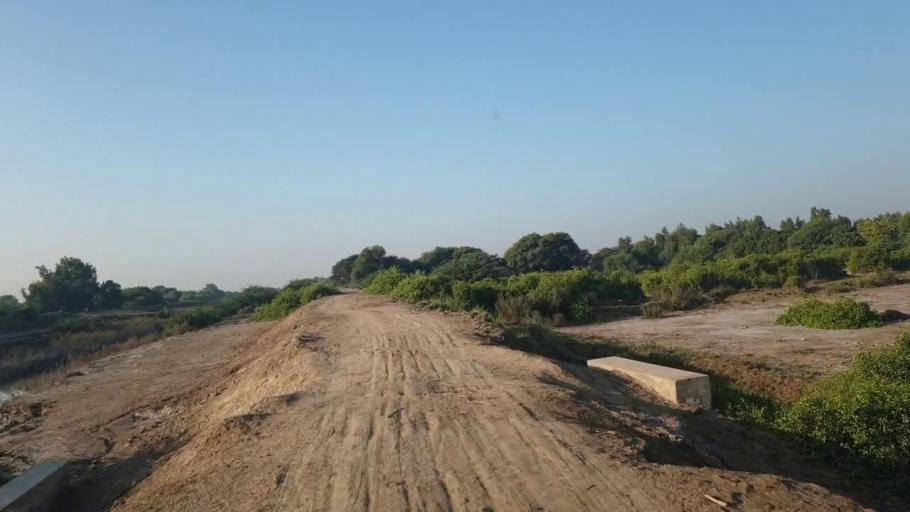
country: PK
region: Sindh
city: Badin
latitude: 24.6213
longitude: 68.7905
